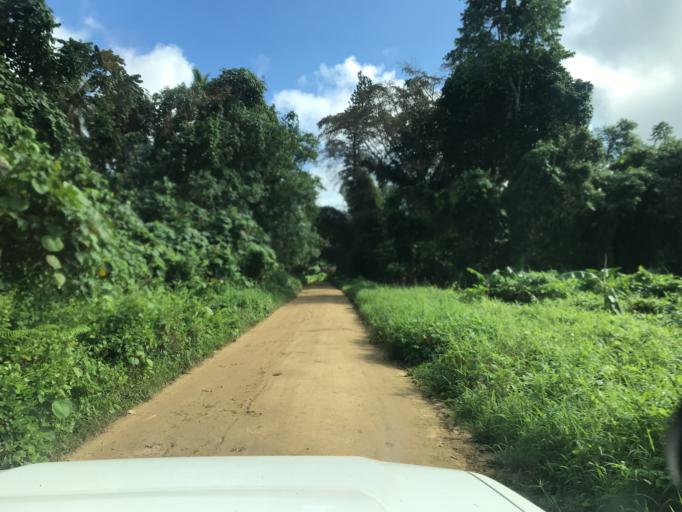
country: VU
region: Sanma
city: Luganville
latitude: -15.5013
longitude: 167.0936
